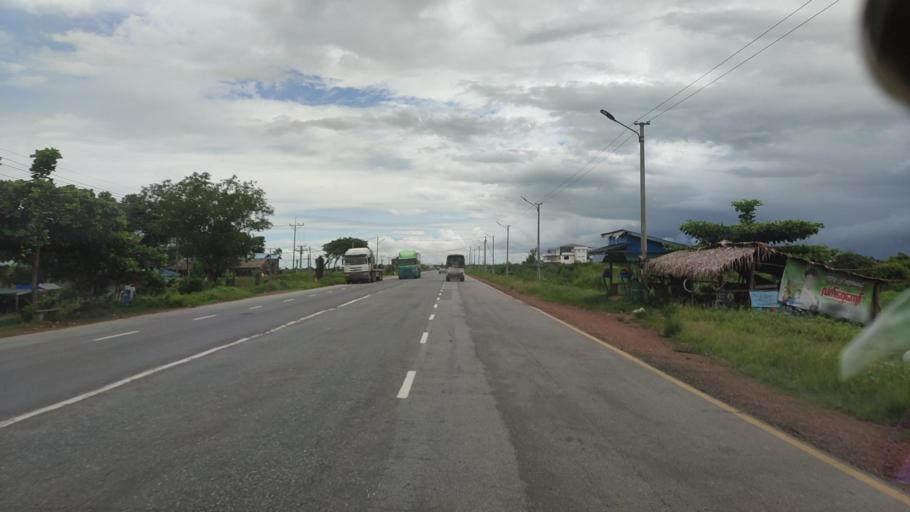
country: MM
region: Bago
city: Bago
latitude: 17.4158
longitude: 96.5215
